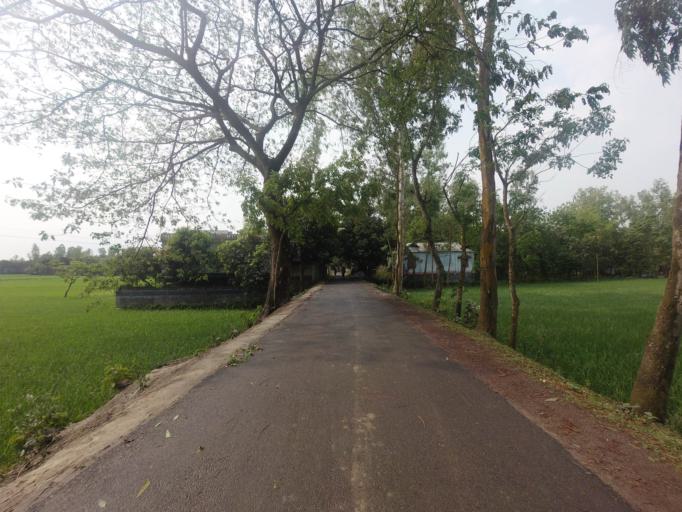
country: BD
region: Rajshahi
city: Sirajganj
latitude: 24.3221
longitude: 89.6743
